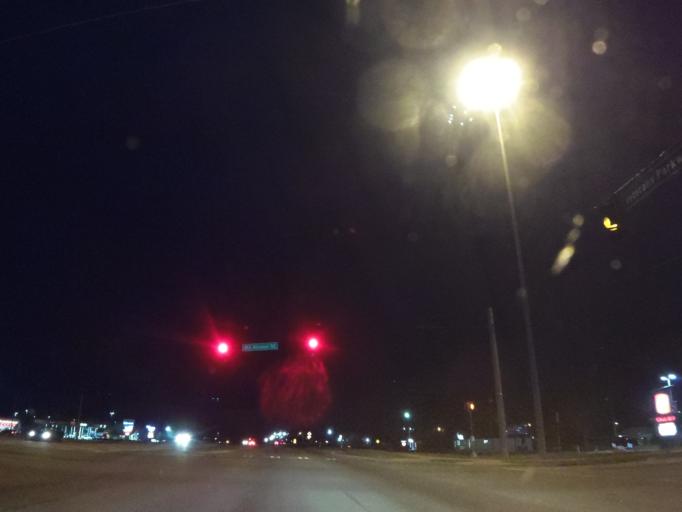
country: US
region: Georgia
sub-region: Colquitt County
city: Moultrie
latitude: 31.1738
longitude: -83.7618
